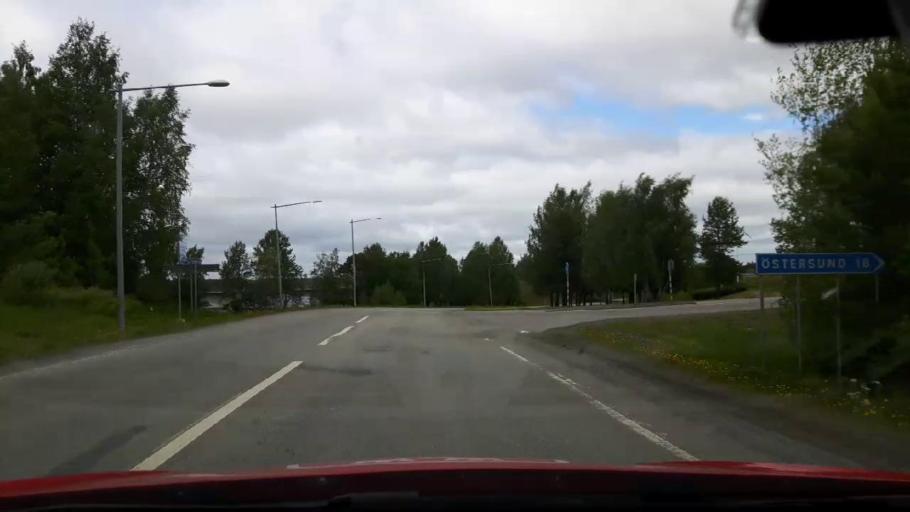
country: SE
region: Jaemtland
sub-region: Krokoms Kommun
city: Krokom
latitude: 63.3141
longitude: 14.4567
